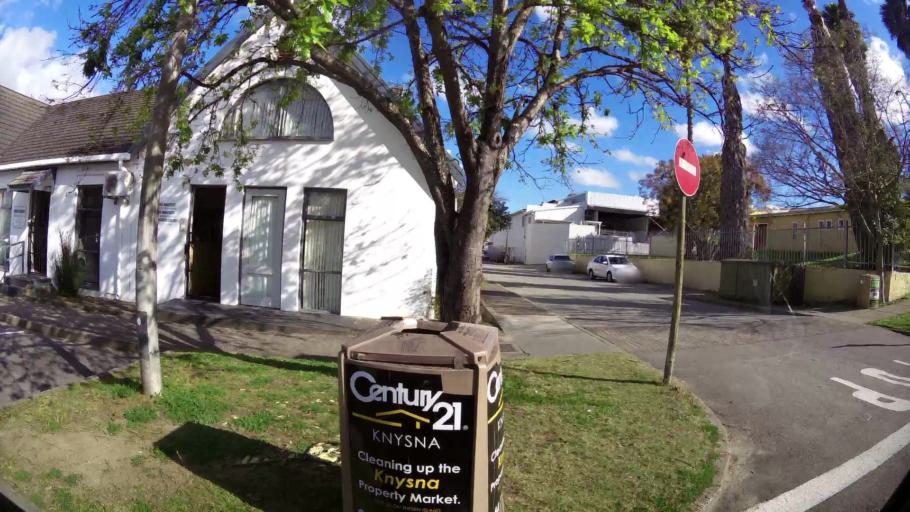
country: ZA
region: Western Cape
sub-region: Eden District Municipality
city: Knysna
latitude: -34.0367
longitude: 23.0508
